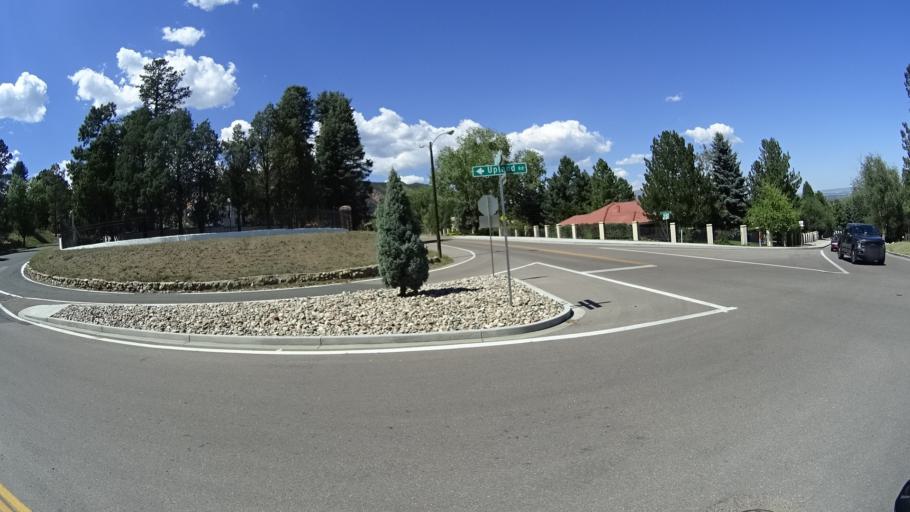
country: US
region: Colorado
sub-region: El Paso County
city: Colorado Springs
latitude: 38.7847
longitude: -104.8559
